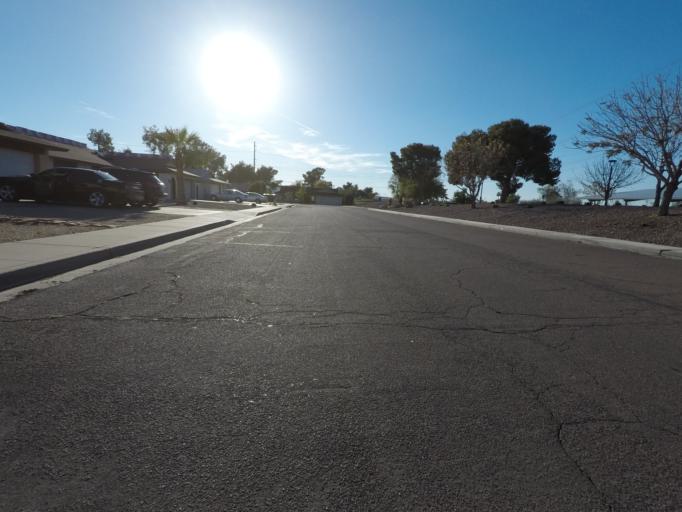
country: US
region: Arizona
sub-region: Maricopa County
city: Guadalupe
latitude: 33.3556
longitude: -111.9301
